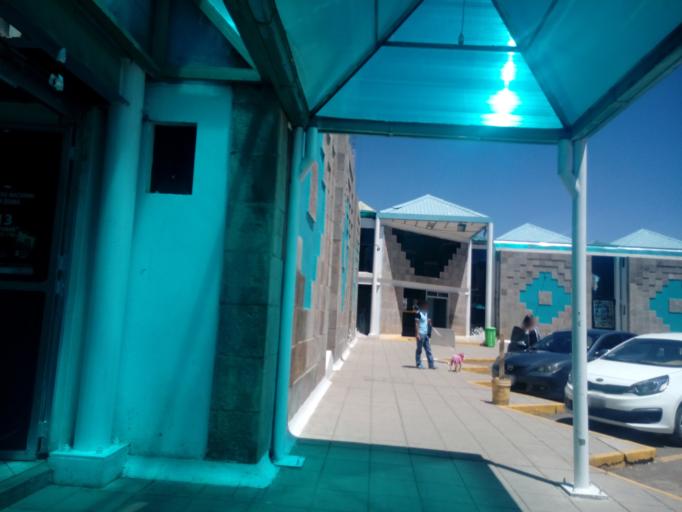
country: PE
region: Puno
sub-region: Provincia de Puno
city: Puno
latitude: -15.8433
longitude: -70.0174
